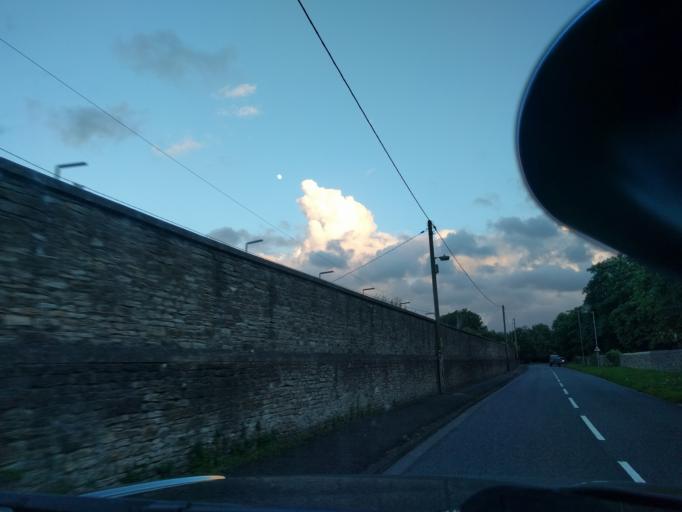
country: GB
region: England
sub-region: Wiltshire
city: Corsham
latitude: 51.4373
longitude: -2.1850
